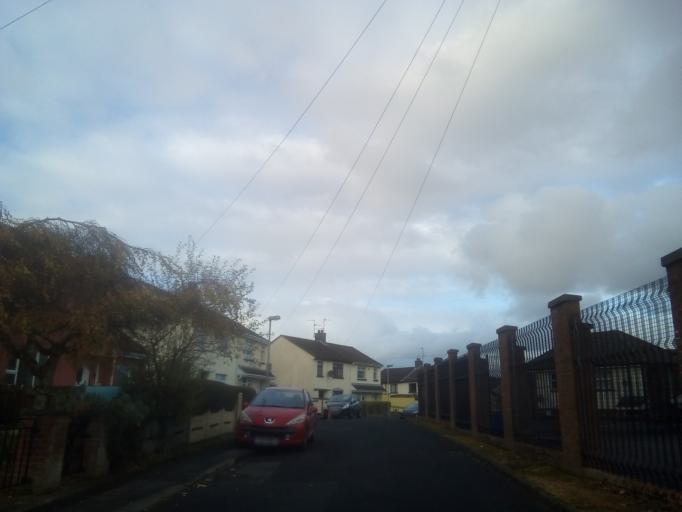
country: GB
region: Northern Ireland
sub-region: City of Derry
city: Derry
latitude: 55.0047
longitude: -7.3268
